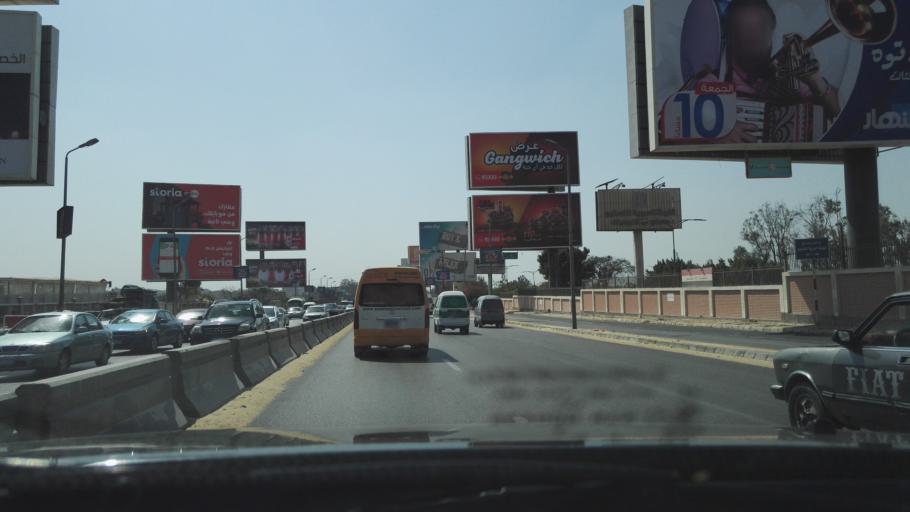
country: EG
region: Muhafazat al Qalyubiyah
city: Al Khankah
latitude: 30.0810
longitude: 31.4008
